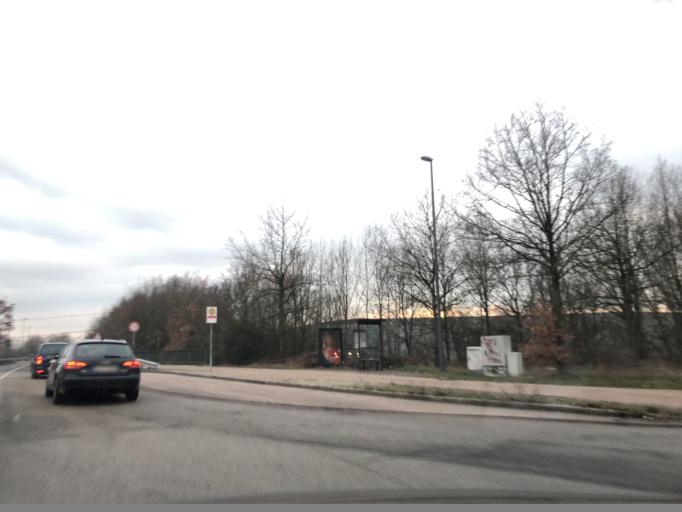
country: DE
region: Lower Saxony
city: Stuhr
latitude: 53.0798
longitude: 8.7370
